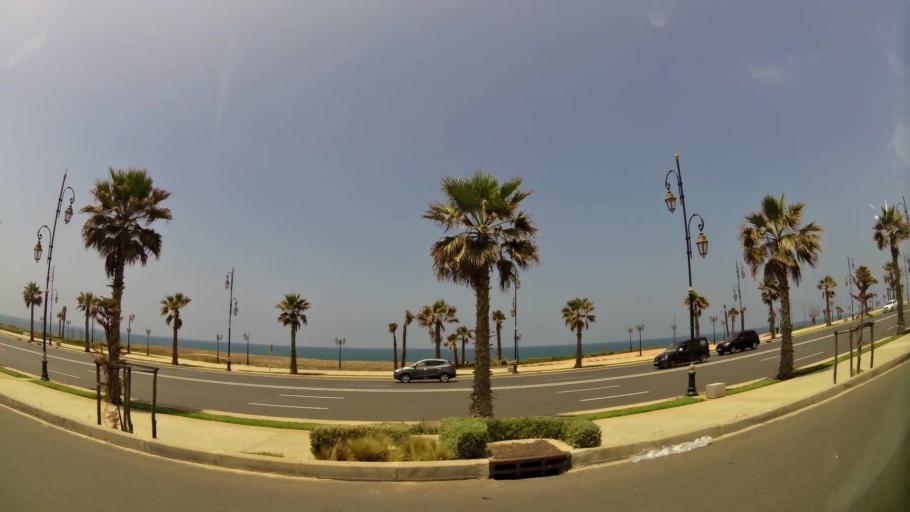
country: MA
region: Rabat-Sale-Zemmour-Zaer
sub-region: Skhirate-Temara
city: Temara
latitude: 33.9719
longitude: -6.9034
